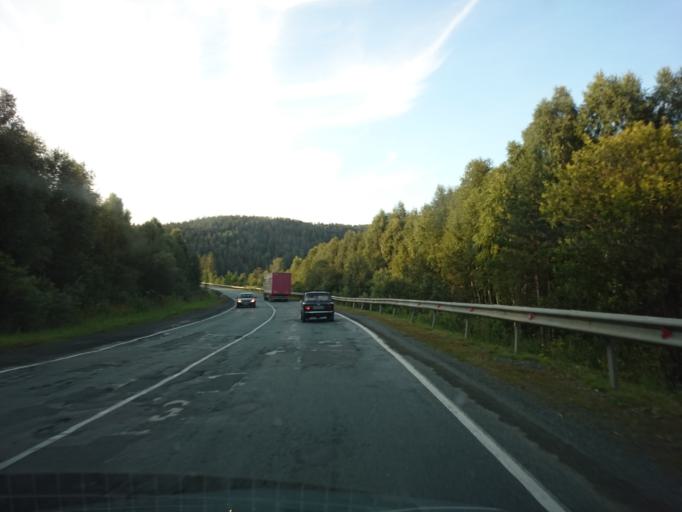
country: RU
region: Bashkortostan
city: Inzer
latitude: 53.9690
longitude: 57.8758
